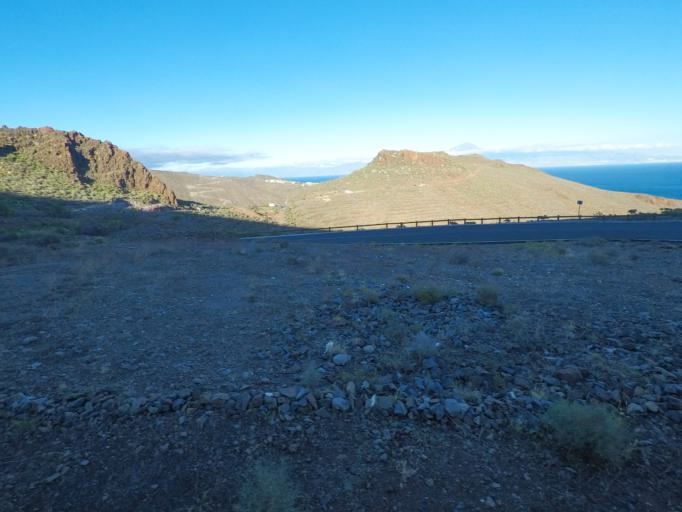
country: ES
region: Canary Islands
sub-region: Provincia de Santa Cruz de Tenerife
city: San Sebastian de la Gomera
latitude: 28.0817
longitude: -17.1274
